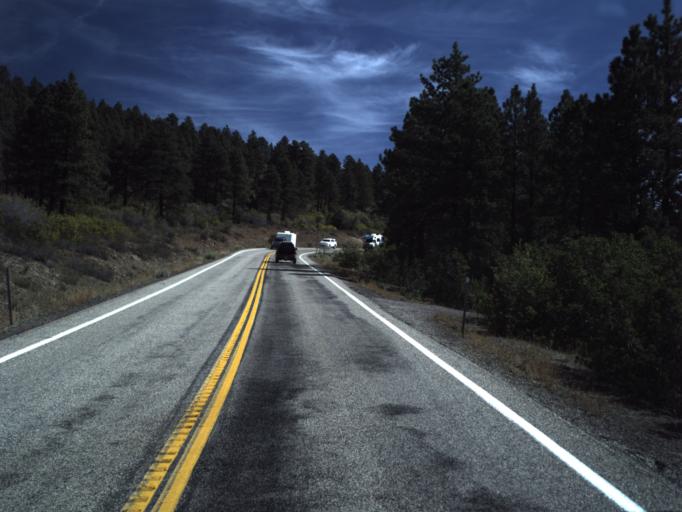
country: US
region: Utah
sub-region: Wayne County
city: Loa
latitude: 37.9924
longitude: -111.4265
